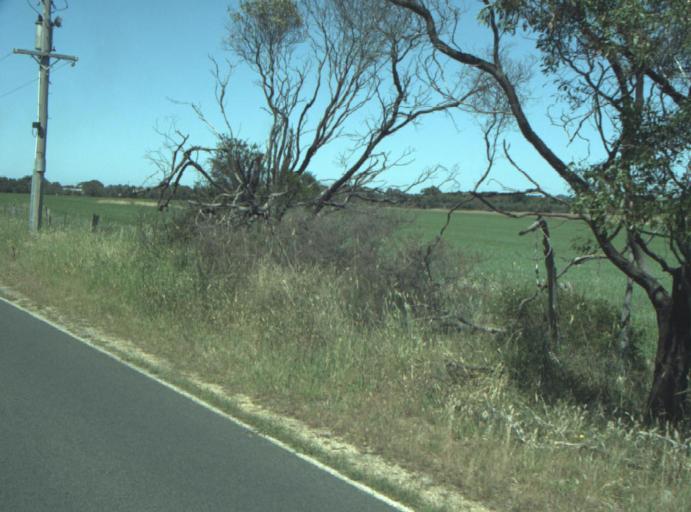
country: AU
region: Victoria
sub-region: Greater Geelong
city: Breakwater
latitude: -38.2276
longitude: 144.3553
